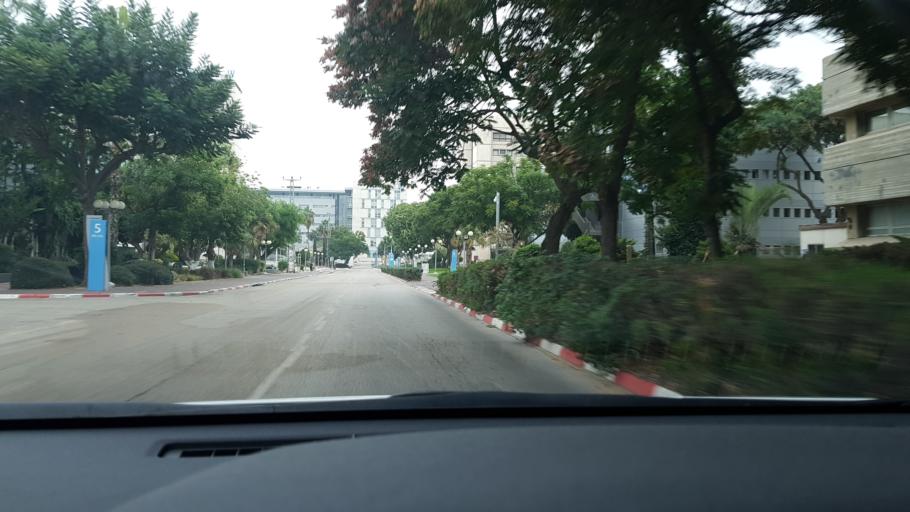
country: IL
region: Central District
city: Ness Ziona
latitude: 31.9148
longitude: 34.8039
